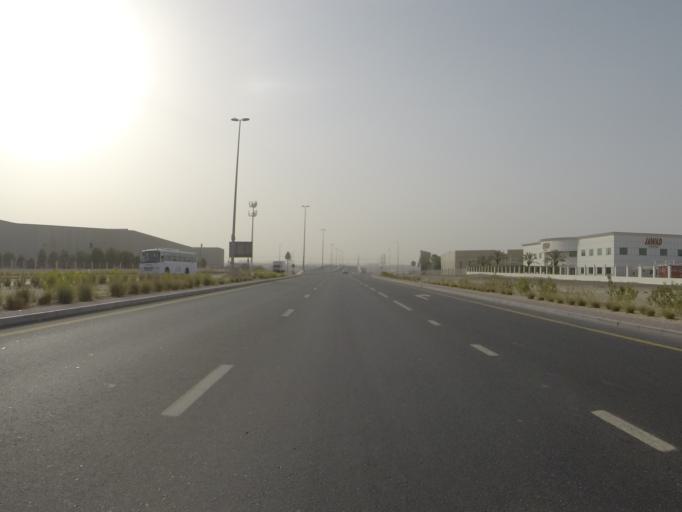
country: AE
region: Dubai
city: Dubai
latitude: 24.9602
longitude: 55.0958
